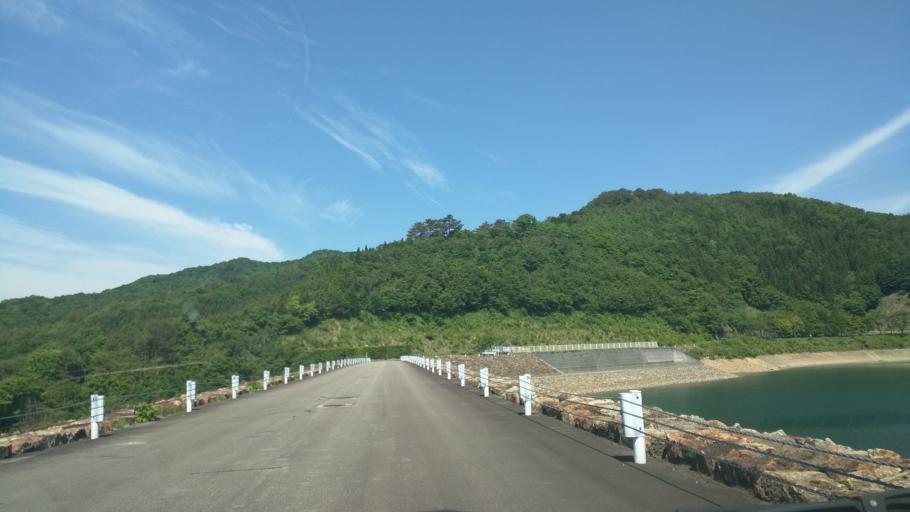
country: JP
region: Fukushima
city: Kitakata
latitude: 37.3427
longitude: 139.8729
